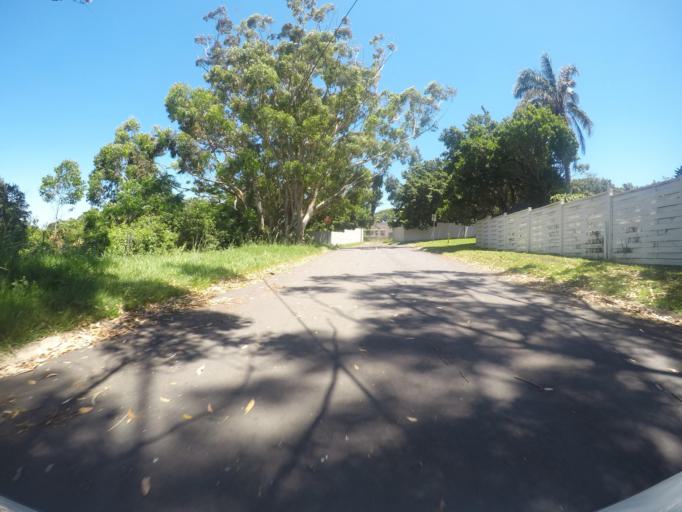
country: ZA
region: Eastern Cape
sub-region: Buffalo City Metropolitan Municipality
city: East London
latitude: -32.9343
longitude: 28.0049
